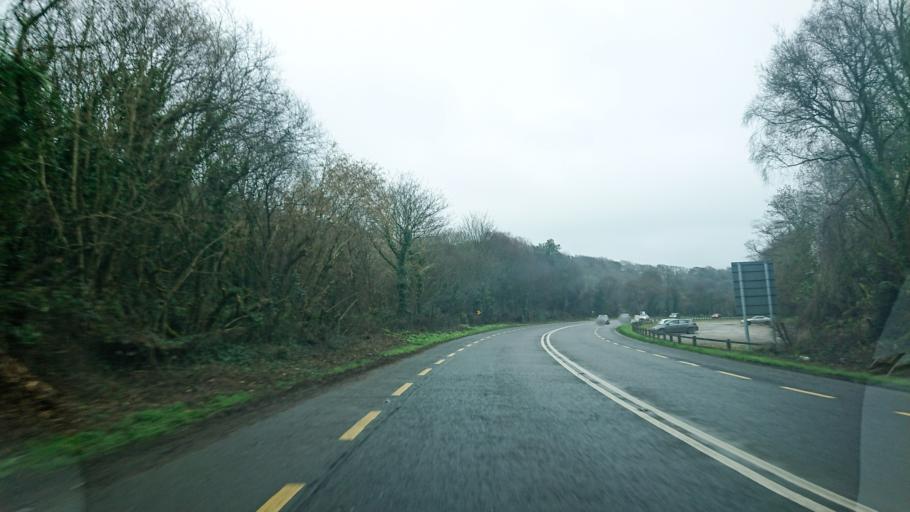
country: IE
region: Munster
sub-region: County Cork
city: Bandon
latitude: 51.7689
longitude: -8.6908
